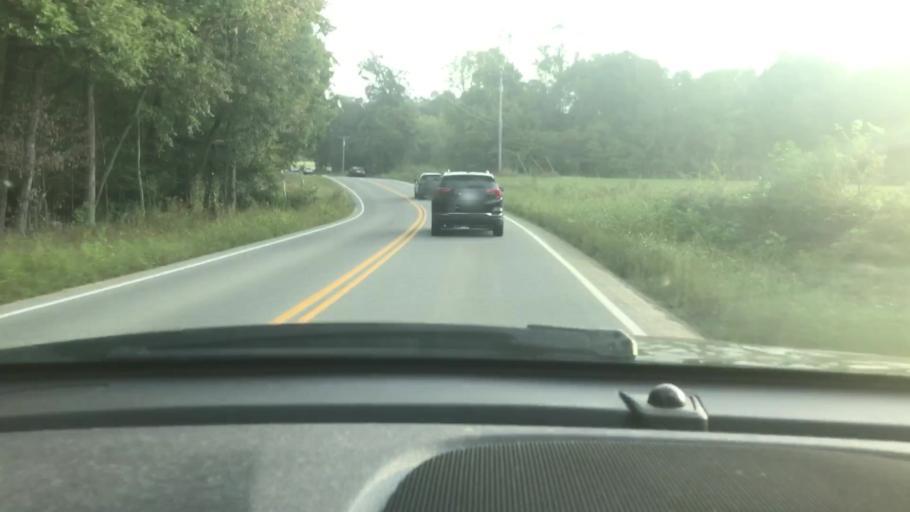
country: US
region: Tennessee
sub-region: Dickson County
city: Charlotte
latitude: 36.2513
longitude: -87.2347
